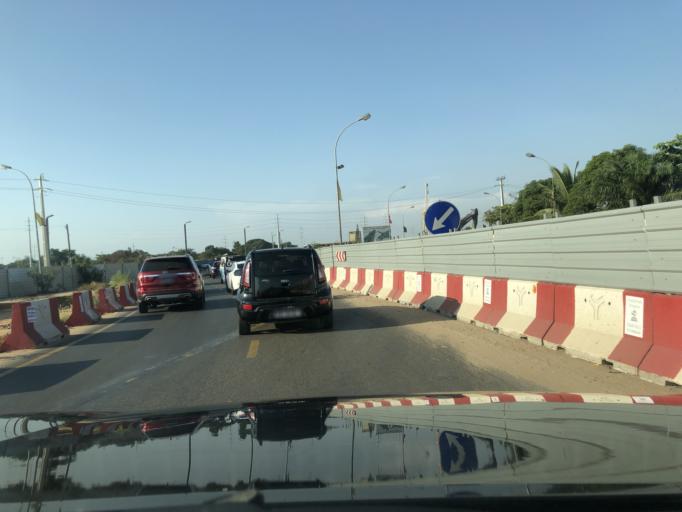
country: AO
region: Luanda
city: Luanda
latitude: -8.9101
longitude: 13.1790
